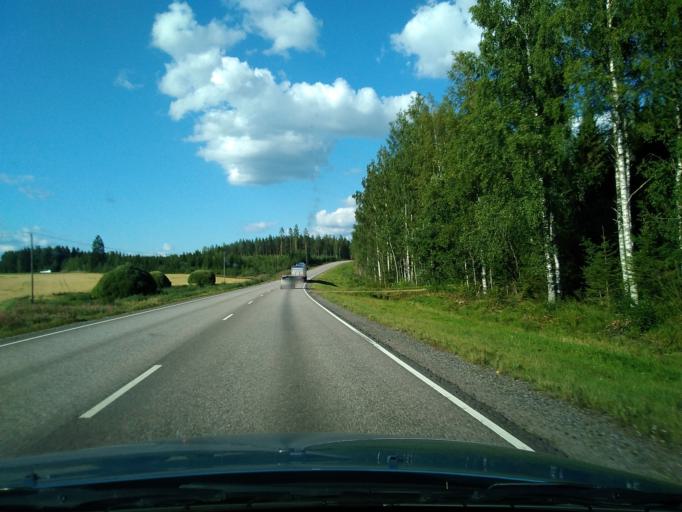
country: FI
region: Central Finland
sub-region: Keuruu
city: Keuruu
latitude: 62.1306
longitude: 24.7363
